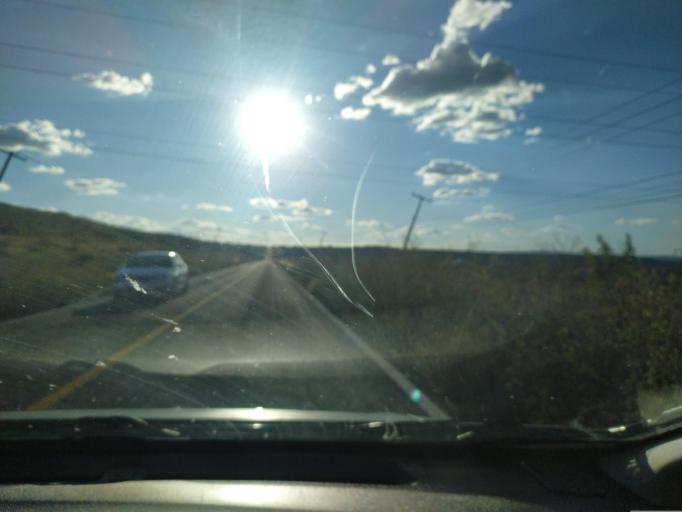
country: MX
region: Guanajuato
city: San Francisco del Rincon
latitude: 21.0340
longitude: -101.9170
